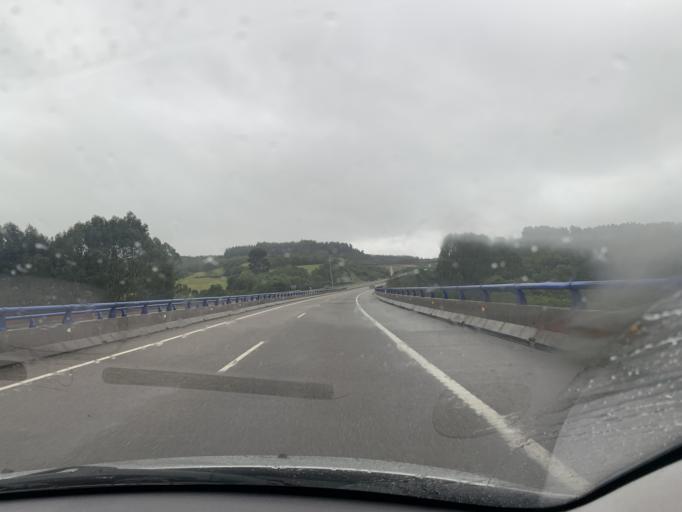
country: ES
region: Galicia
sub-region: Provincia de Lugo
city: Abadin
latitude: 43.3640
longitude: -7.4506
